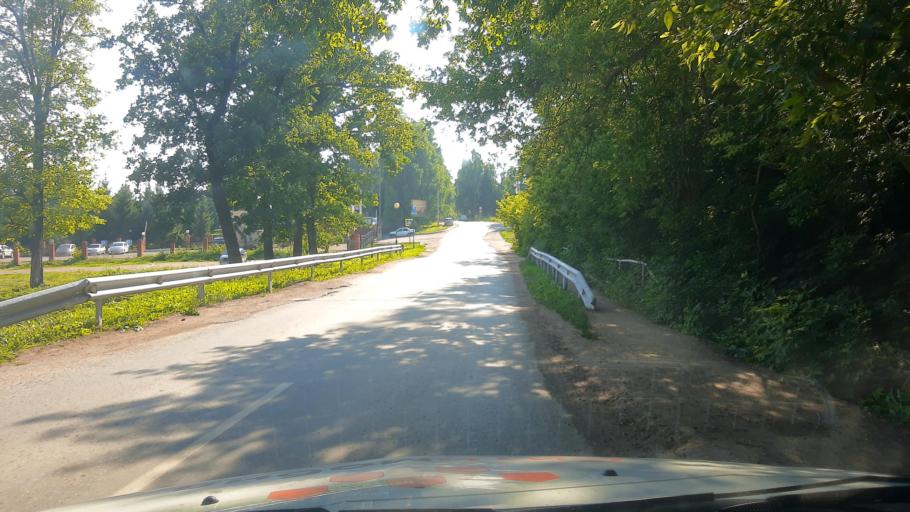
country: RU
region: Bashkortostan
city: Avdon
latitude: 54.6159
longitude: 55.6414
